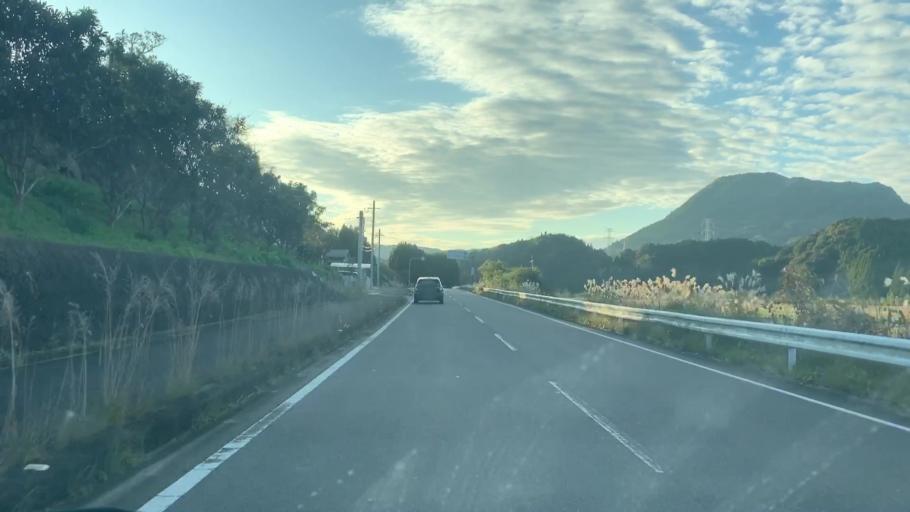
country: JP
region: Saga Prefecture
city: Karatsu
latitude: 33.3514
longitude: 129.9990
